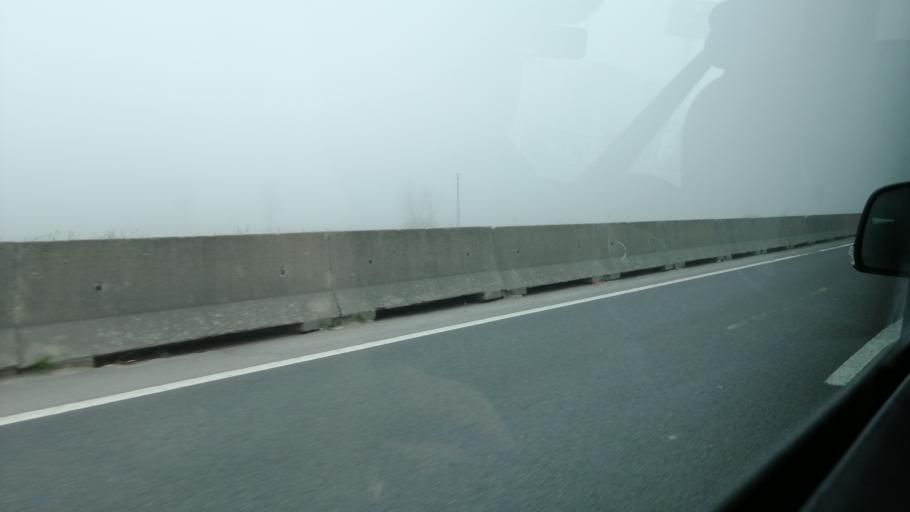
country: TR
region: Yalova
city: Taskopru
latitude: 40.6799
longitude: 29.3703
